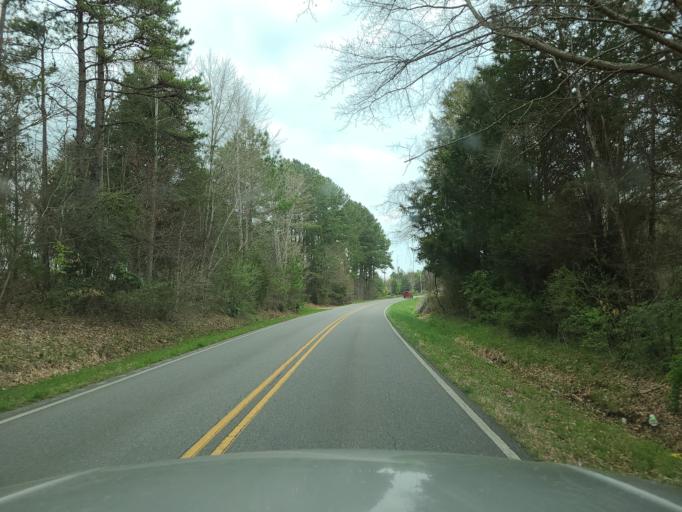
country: US
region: North Carolina
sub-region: Cleveland County
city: Shelby
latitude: 35.3353
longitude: -81.5356
